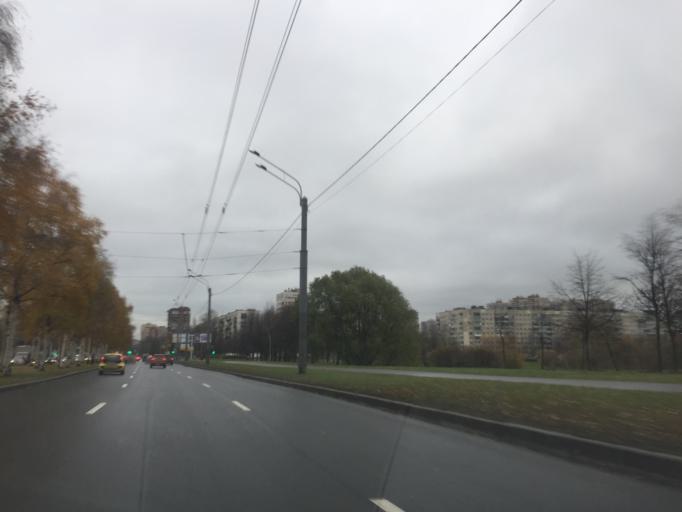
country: RU
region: Leningrad
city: Akademicheskoe
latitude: 60.0287
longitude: 30.3897
